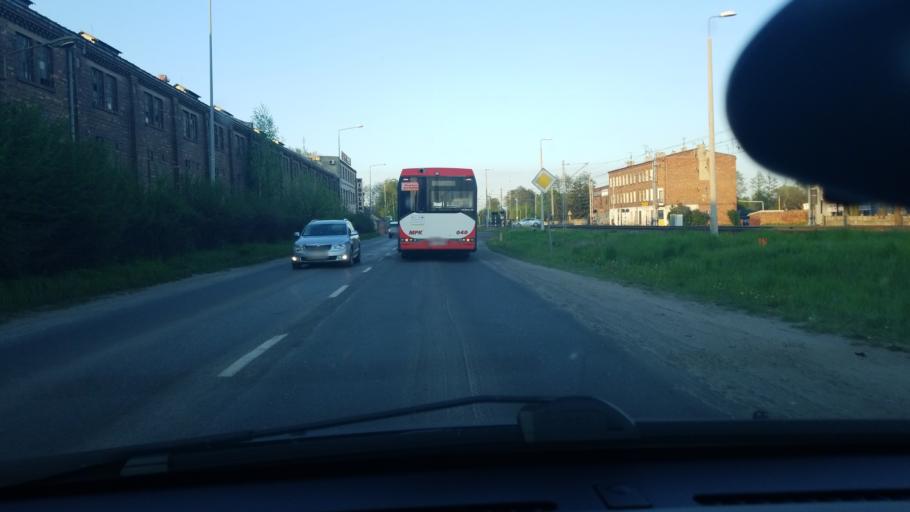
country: PL
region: Silesian Voivodeship
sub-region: Powiat klobucki
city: Kalej
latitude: 50.7952
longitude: 19.0453
